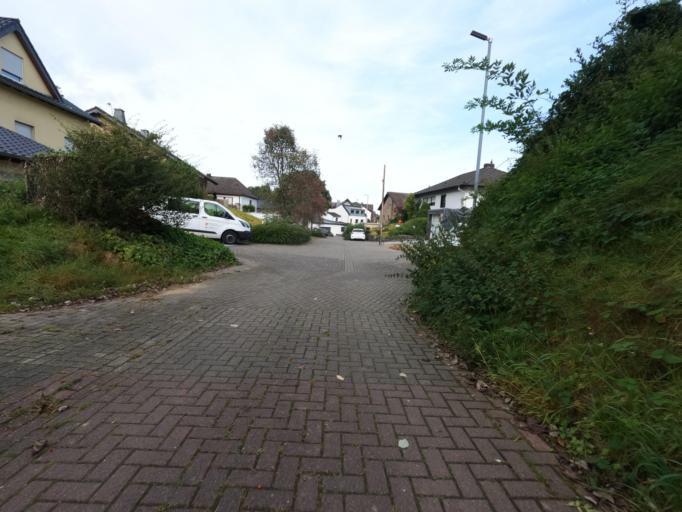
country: DE
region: North Rhine-Westphalia
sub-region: Regierungsbezirk Koln
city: Linnich
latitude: 50.9565
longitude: 6.2212
